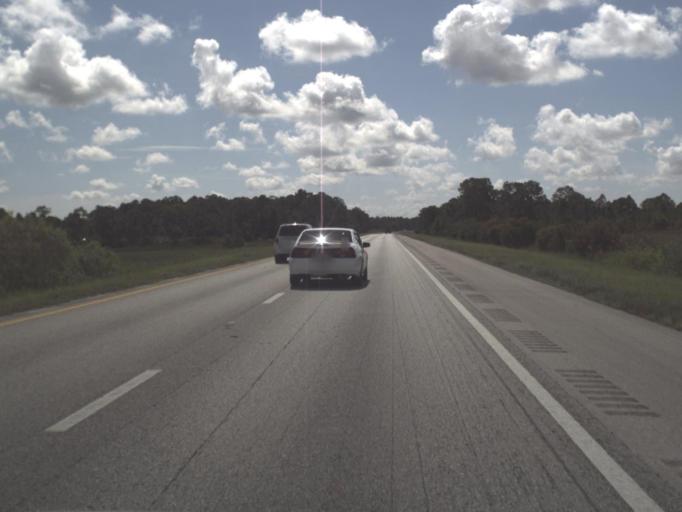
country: US
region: Florida
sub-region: Lee County
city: Suncoast Estates
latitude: 26.8015
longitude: -81.9197
